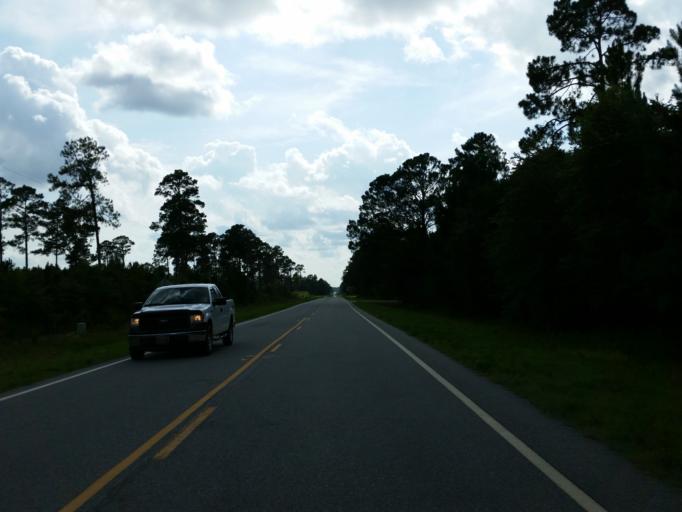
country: US
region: Georgia
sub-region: Lee County
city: Leesburg
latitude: 31.7284
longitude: -83.9659
